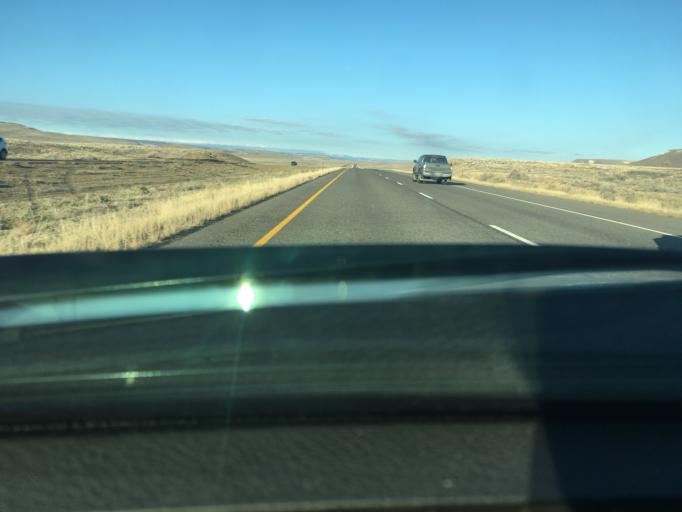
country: US
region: Colorado
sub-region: Delta County
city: Delta
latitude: 38.7606
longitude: -108.1943
